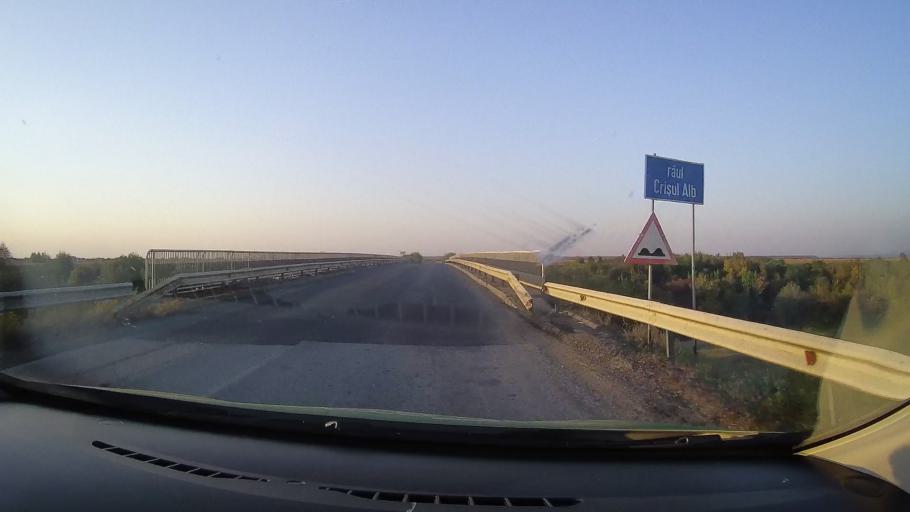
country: RO
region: Arad
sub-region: Comuna Ineu
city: Ineu
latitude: 46.4310
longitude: 21.8598
